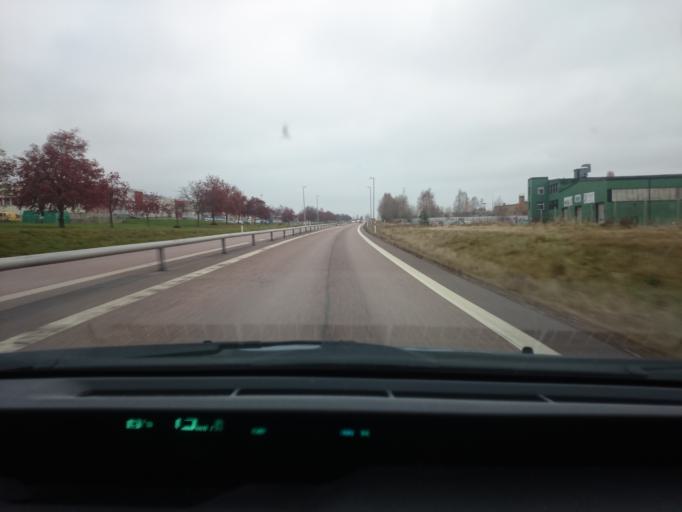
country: SE
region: Dalarna
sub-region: Hedemora Kommun
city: Hedemora
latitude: 60.2889
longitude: 15.9864
